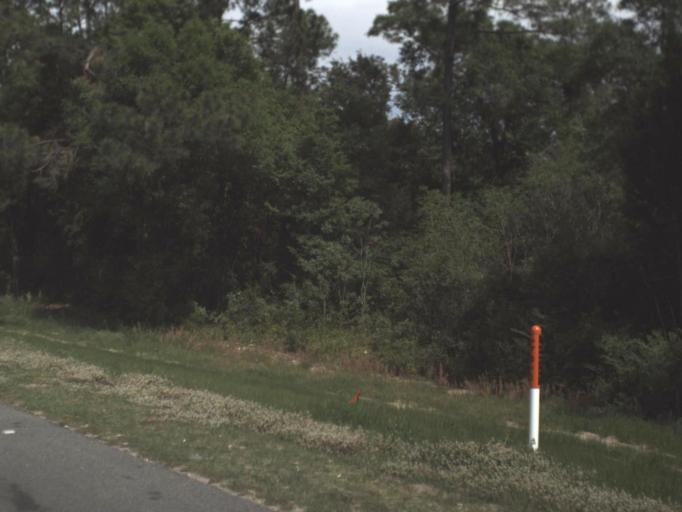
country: US
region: Florida
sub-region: Santa Rosa County
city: Milton
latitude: 30.6251
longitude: -87.0334
